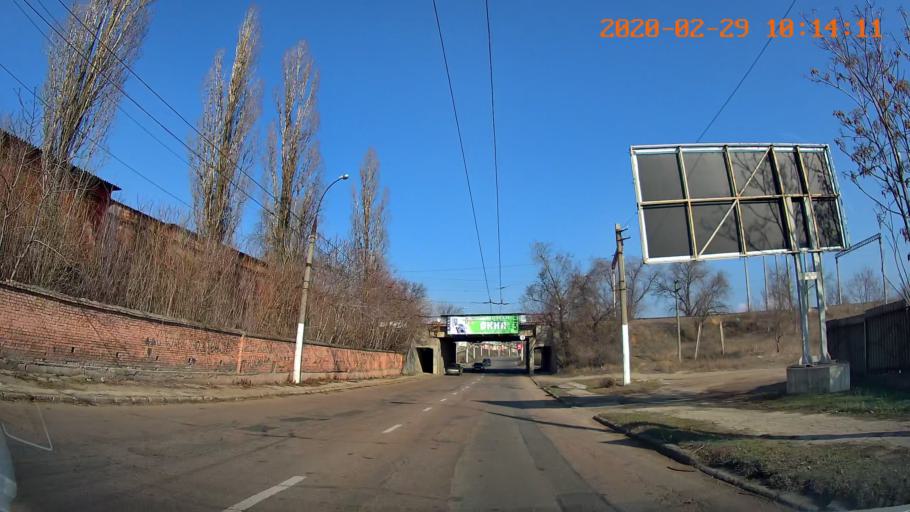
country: MD
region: Telenesti
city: Tiraspolul Nou
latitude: 46.8446
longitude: 29.6442
